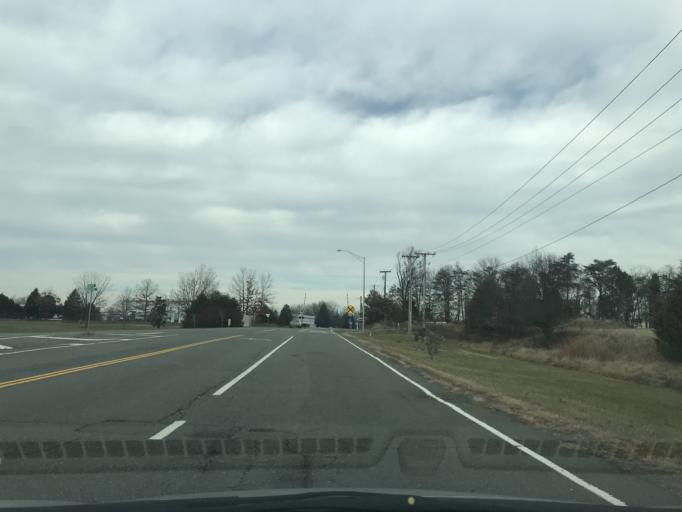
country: US
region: Virginia
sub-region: City of Manassas
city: Manassas
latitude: 38.7331
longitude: -77.5171
